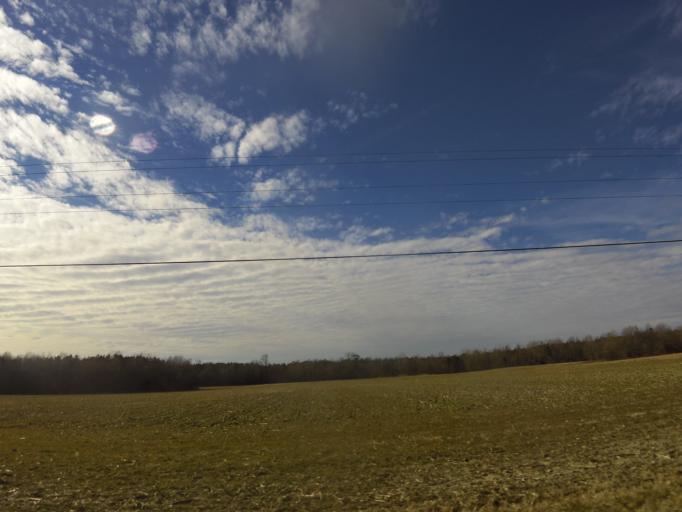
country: US
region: Virginia
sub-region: City of Franklin
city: Franklin
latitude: 36.7381
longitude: -76.8766
